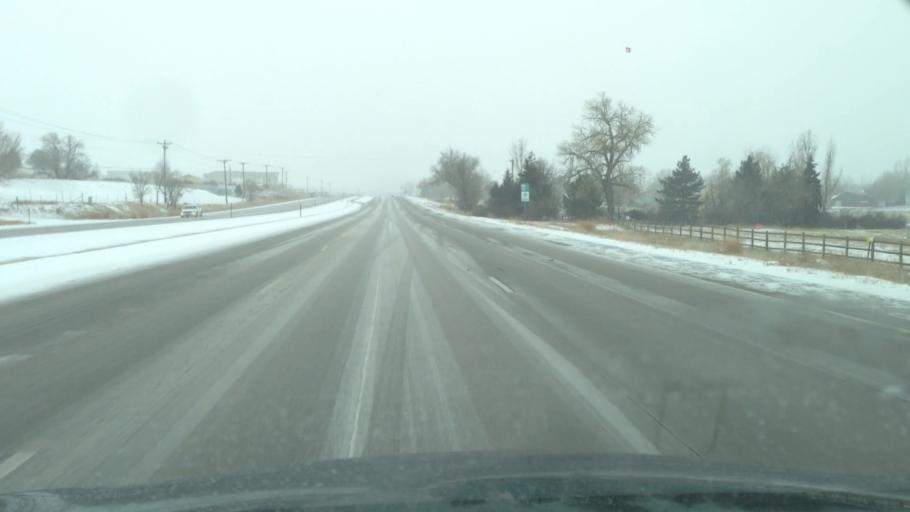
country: US
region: Colorado
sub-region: Douglas County
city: Stonegate
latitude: 39.5659
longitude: -104.7851
